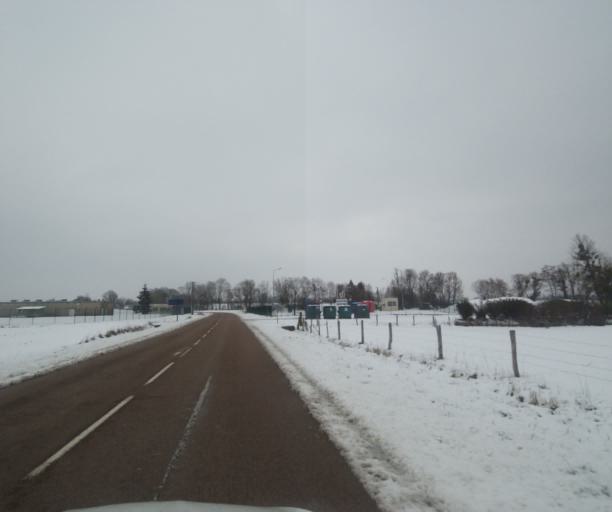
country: FR
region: Champagne-Ardenne
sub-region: Departement de la Haute-Marne
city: Villiers-en-Lieu
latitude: 48.5928
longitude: 4.8518
